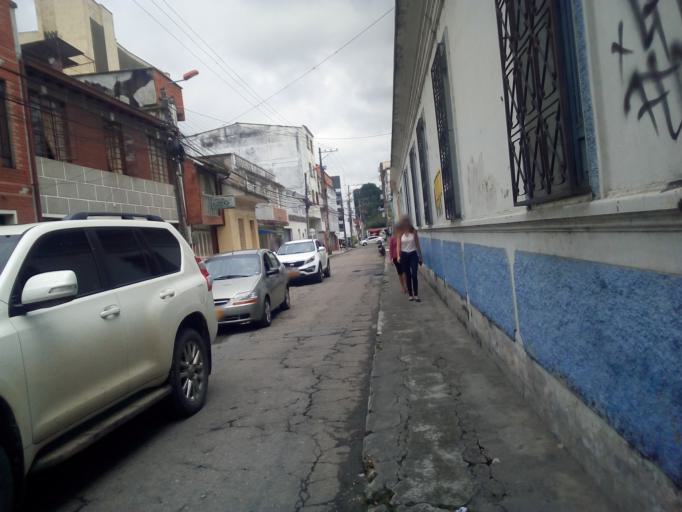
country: CO
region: Tolima
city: Ibague
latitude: 4.4458
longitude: -75.2440
